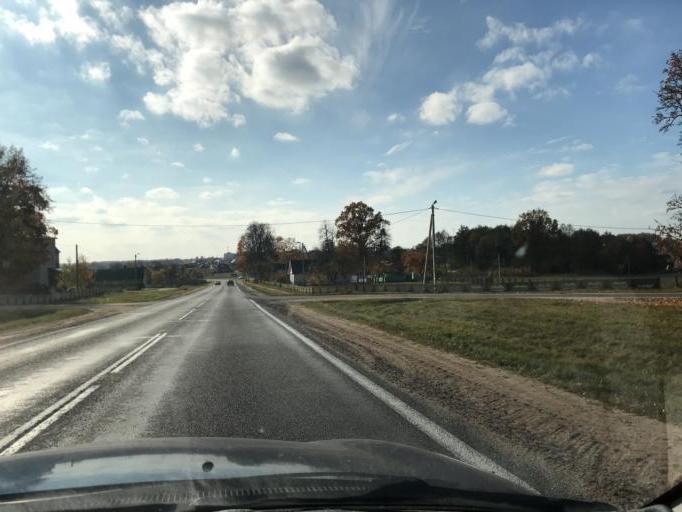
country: BY
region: Grodnenskaya
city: Voranava
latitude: 54.1597
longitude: 25.3270
